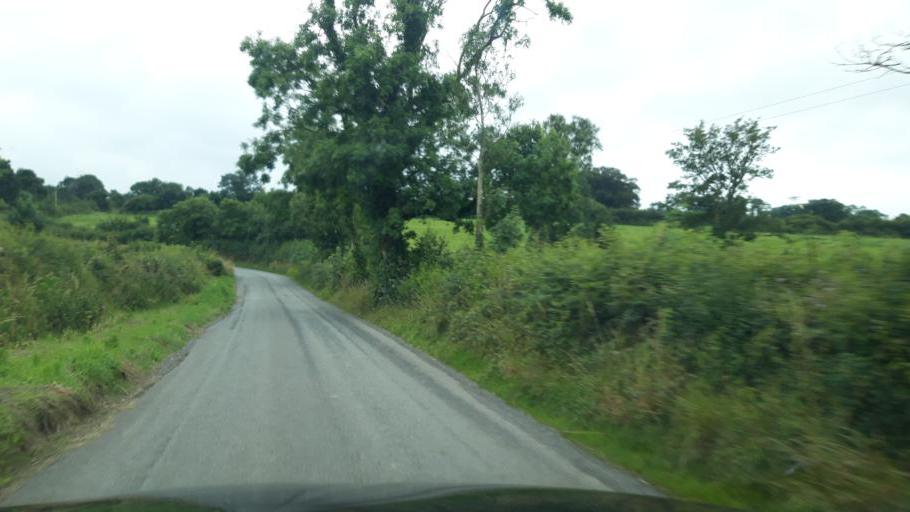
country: IE
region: Leinster
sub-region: Kilkenny
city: Ballyragget
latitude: 52.7040
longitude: -7.4094
